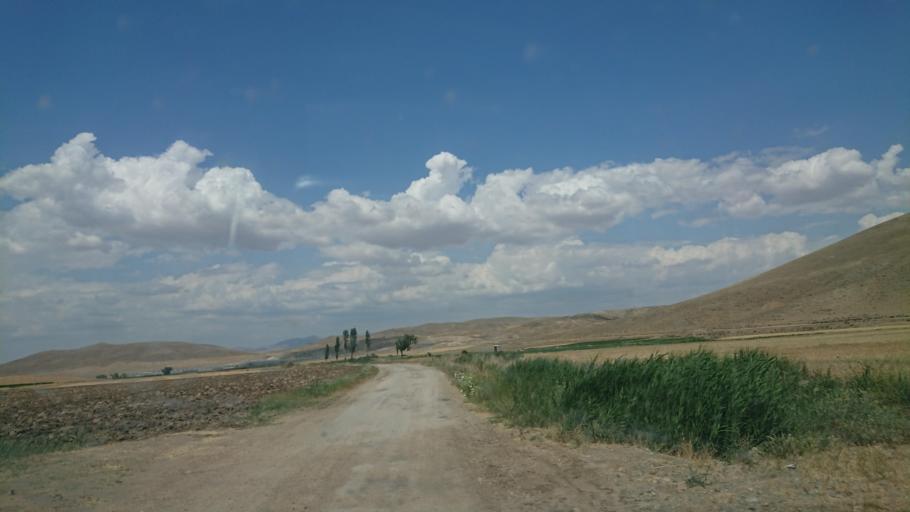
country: TR
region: Aksaray
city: Sariyahsi
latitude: 38.9857
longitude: 33.9077
